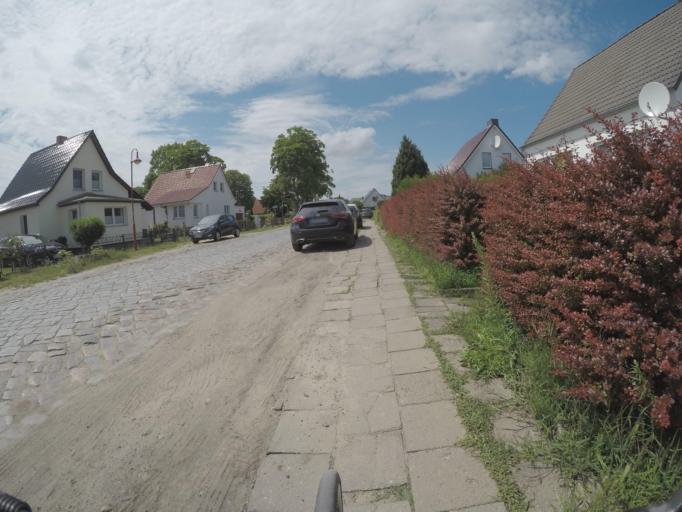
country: DE
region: Mecklenburg-Vorpommern
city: Altefahr
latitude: 54.3285
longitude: 13.1337
